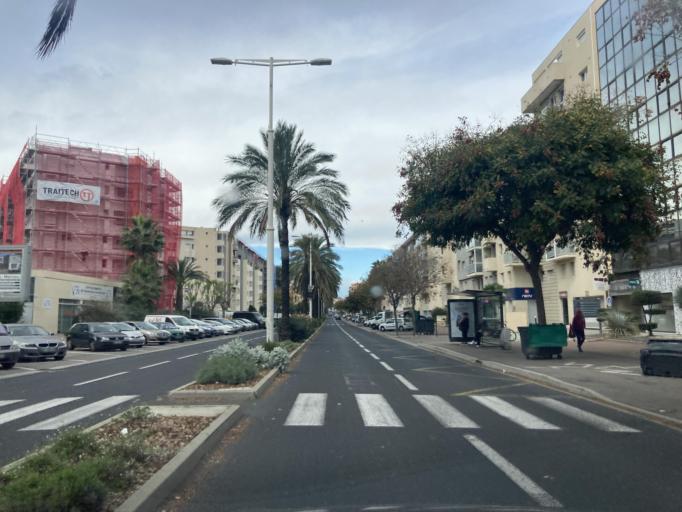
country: FR
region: Languedoc-Roussillon
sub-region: Departement des Pyrenees-Orientales
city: Perpignan
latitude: 42.6871
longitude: 2.9063
